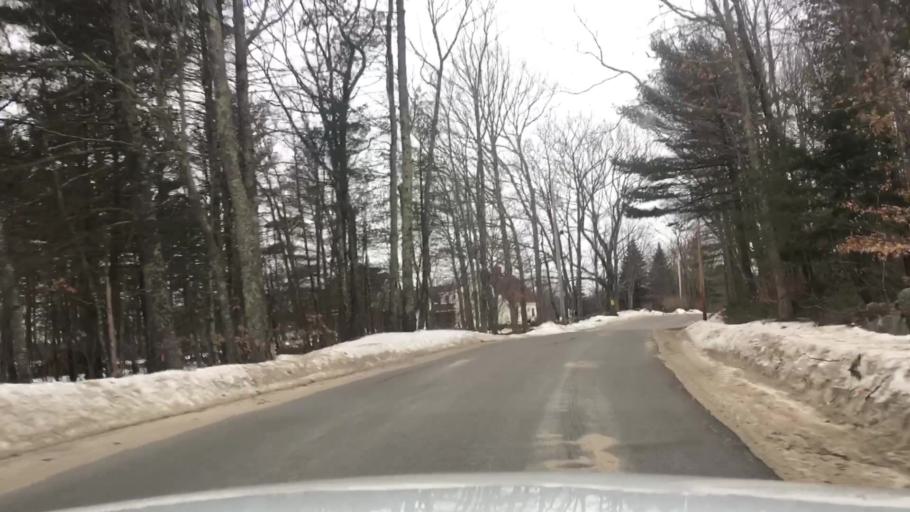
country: US
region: Maine
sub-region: York County
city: Shapleigh
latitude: 43.5042
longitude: -70.8271
